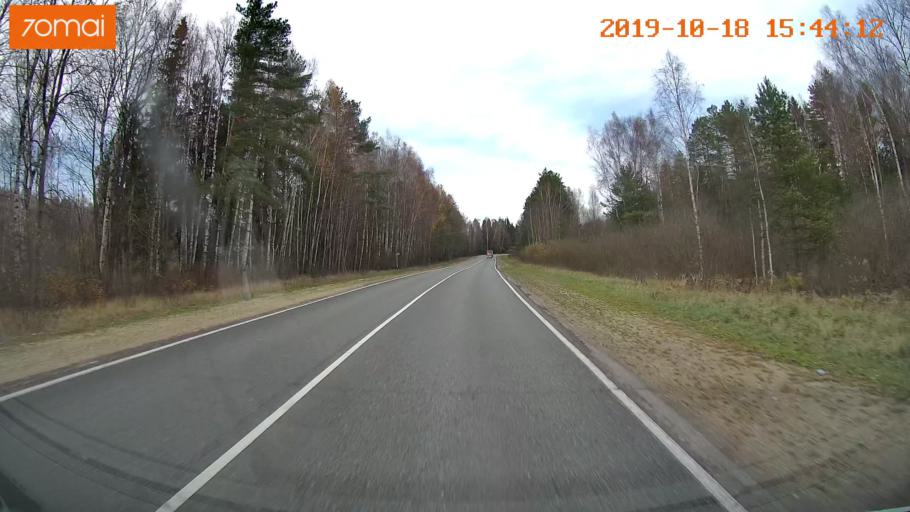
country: RU
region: Vladimir
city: Golovino
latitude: 55.9784
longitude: 40.5473
